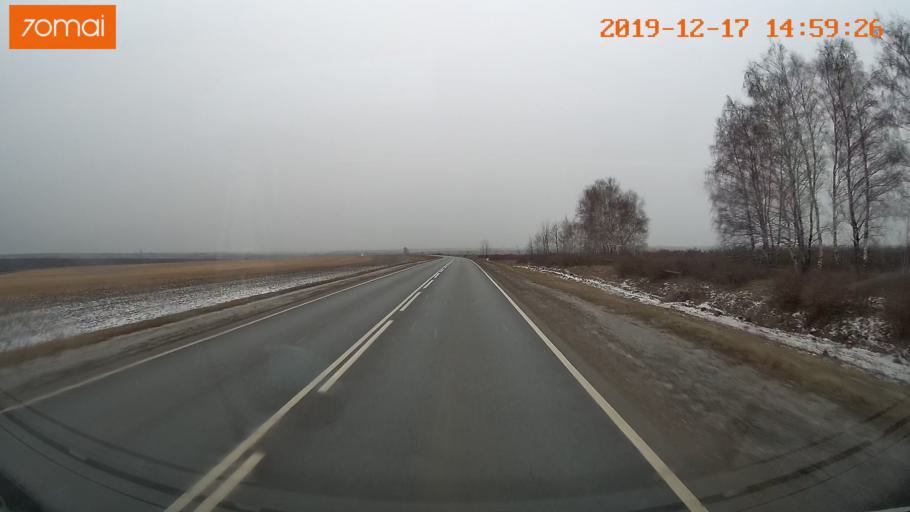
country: RU
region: Rjazan
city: Zakharovo
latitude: 54.3041
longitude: 39.2049
